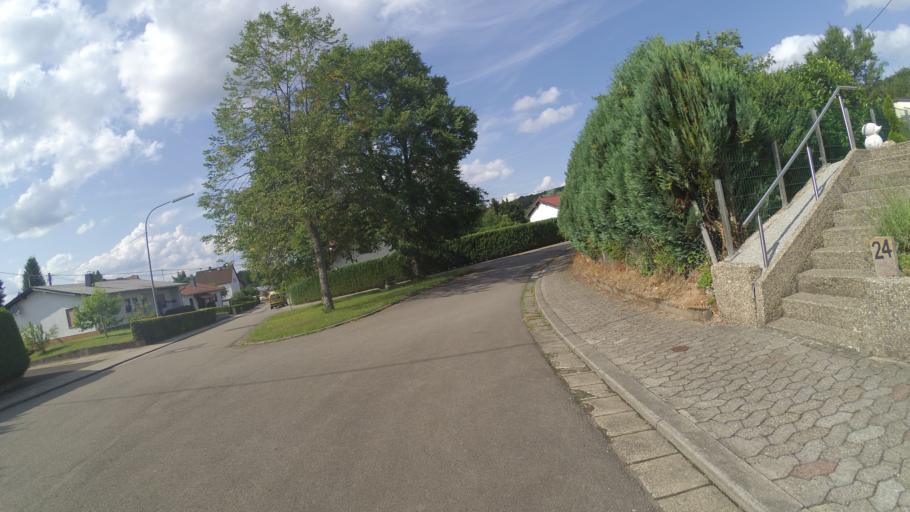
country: DE
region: Saarland
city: Nohfelden
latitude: 49.5782
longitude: 7.1491
